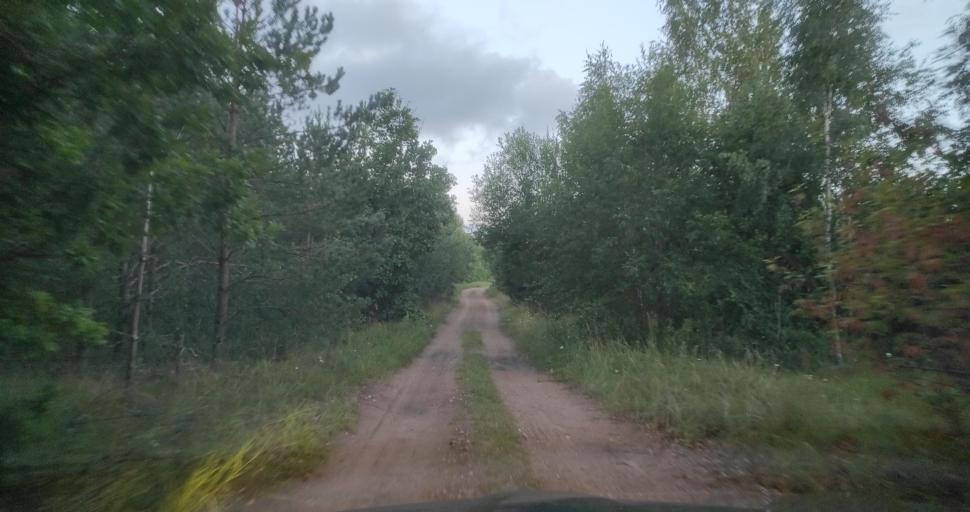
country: LV
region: Kuldigas Rajons
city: Kuldiga
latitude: 57.0602
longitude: 21.8657
